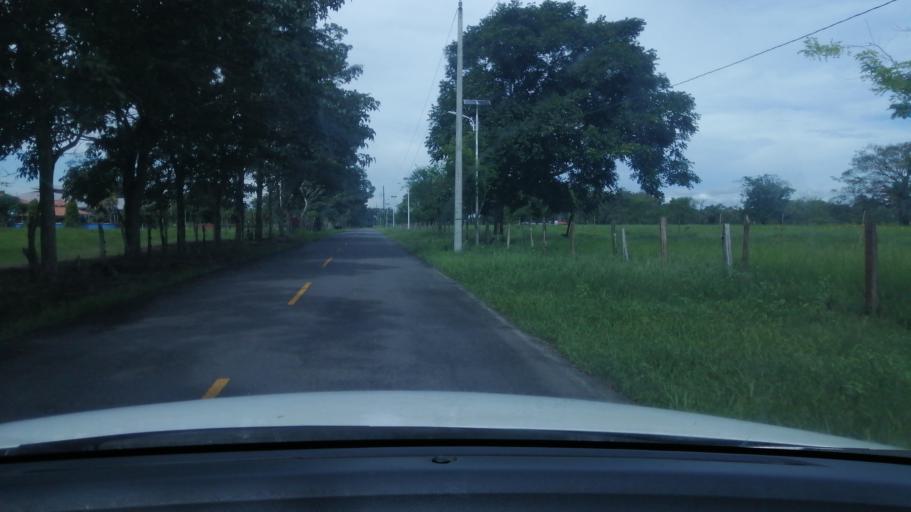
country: PA
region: Chiriqui
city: David
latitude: 8.4223
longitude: -82.4532
